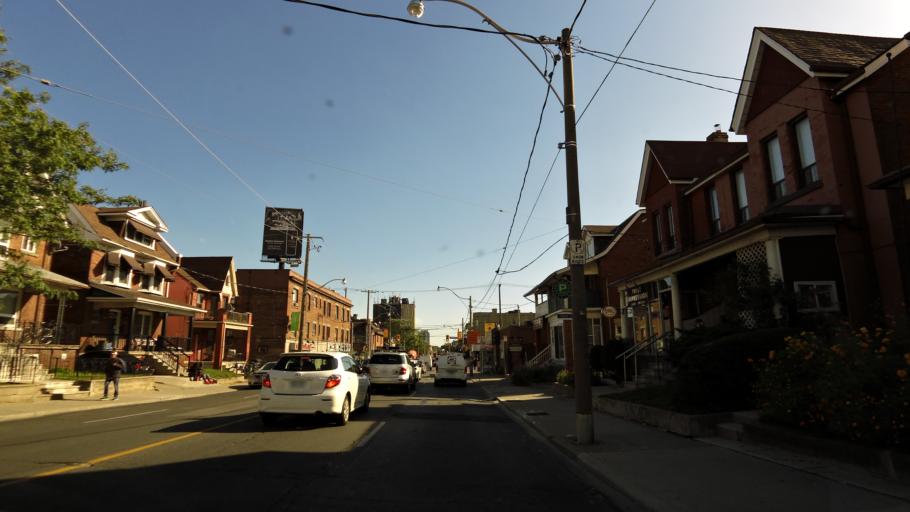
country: CA
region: Ontario
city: Toronto
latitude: 43.6532
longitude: -79.4329
